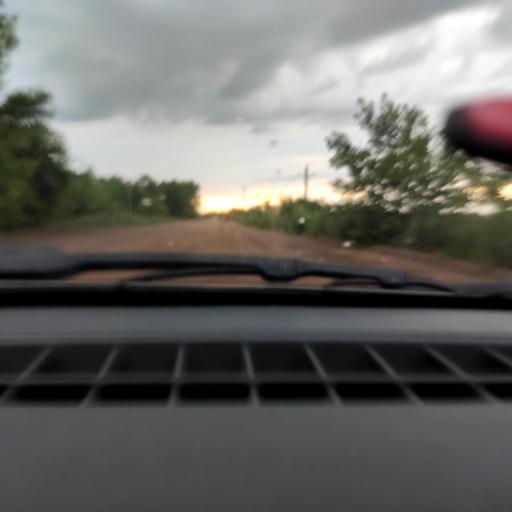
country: RU
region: Bashkortostan
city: Blagoveshchensk
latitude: 54.9183
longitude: 55.9805
